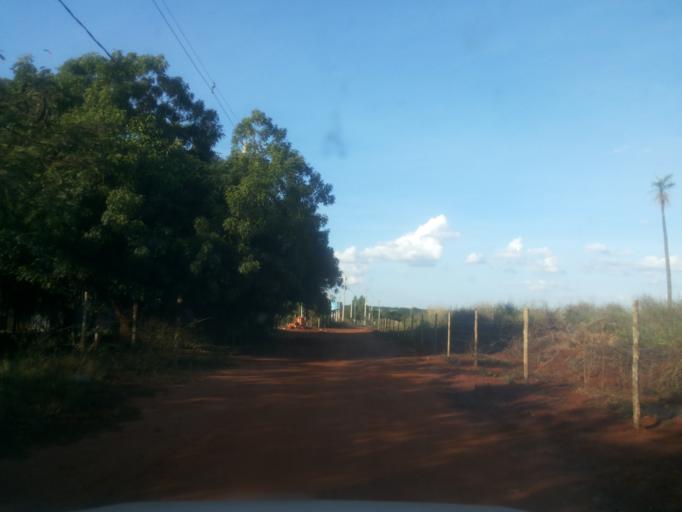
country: BR
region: Minas Gerais
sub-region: Santa Vitoria
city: Santa Vitoria
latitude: -18.9849
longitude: -50.3678
